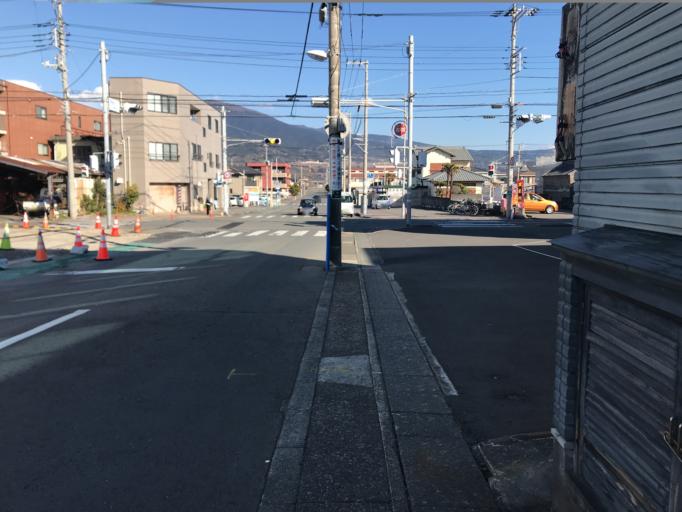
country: JP
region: Shizuoka
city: Numazu
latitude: 35.1261
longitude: 138.7945
